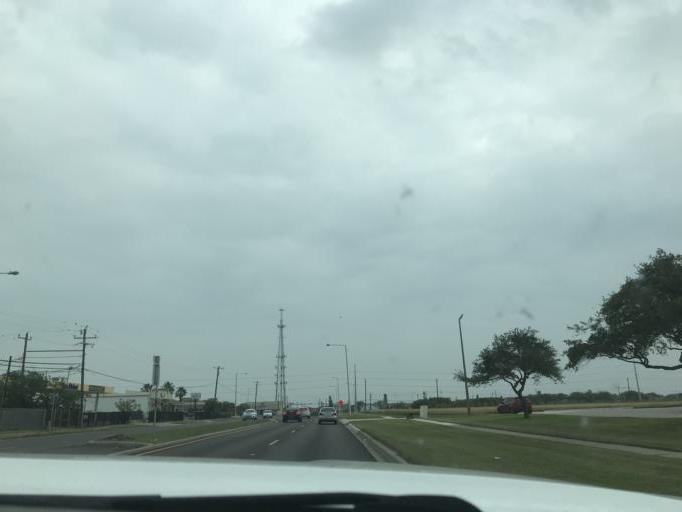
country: US
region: Texas
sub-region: Nueces County
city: Corpus Christi
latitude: 27.6729
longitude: -97.3586
